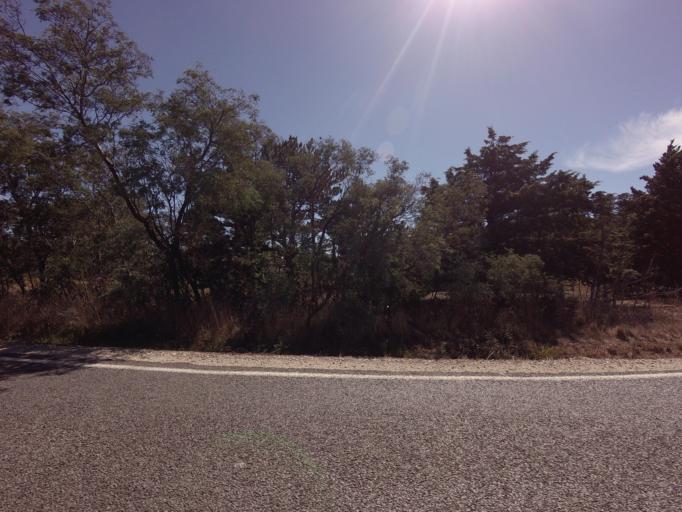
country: AU
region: Tasmania
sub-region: Northern Midlands
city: Evandale
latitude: -41.7866
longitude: 147.7158
